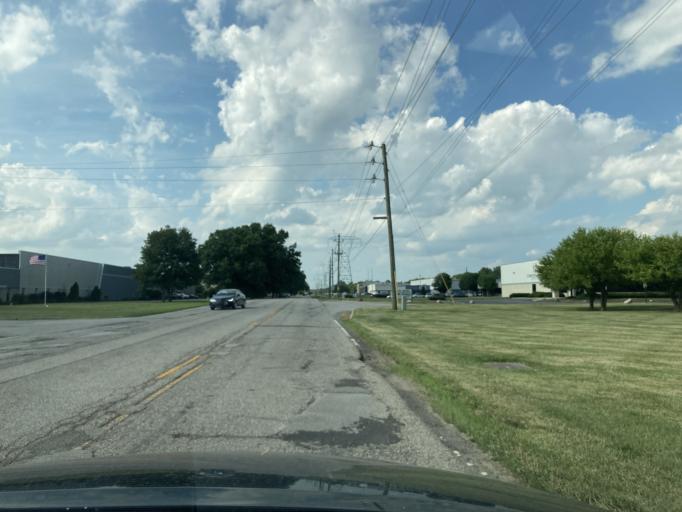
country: US
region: Indiana
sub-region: Marion County
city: Meridian Hills
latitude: 39.8758
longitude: -86.2316
